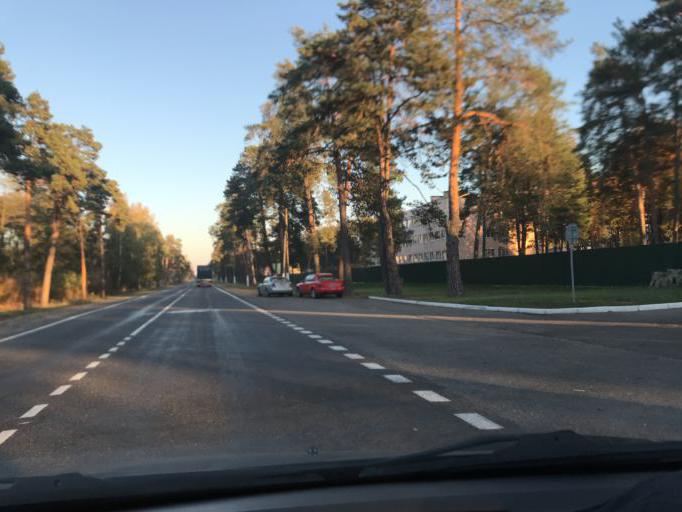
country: BY
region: Minsk
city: Staryya Darohi
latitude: 53.0352
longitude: 28.2293
